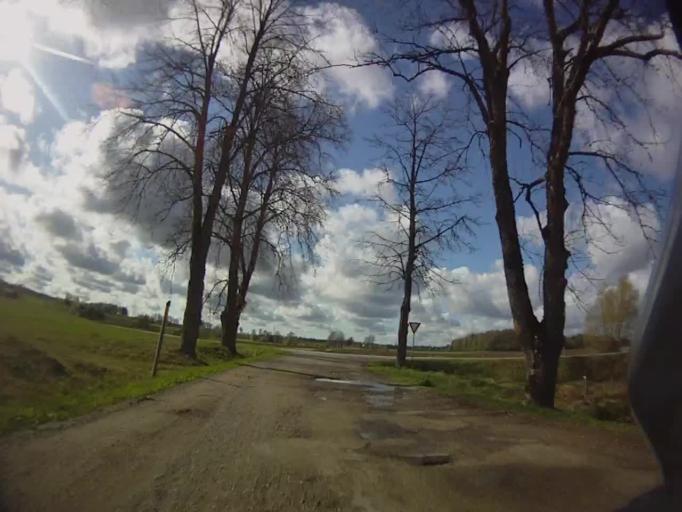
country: LV
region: Krimulda
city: Ragana
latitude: 57.1645
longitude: 24.7681
